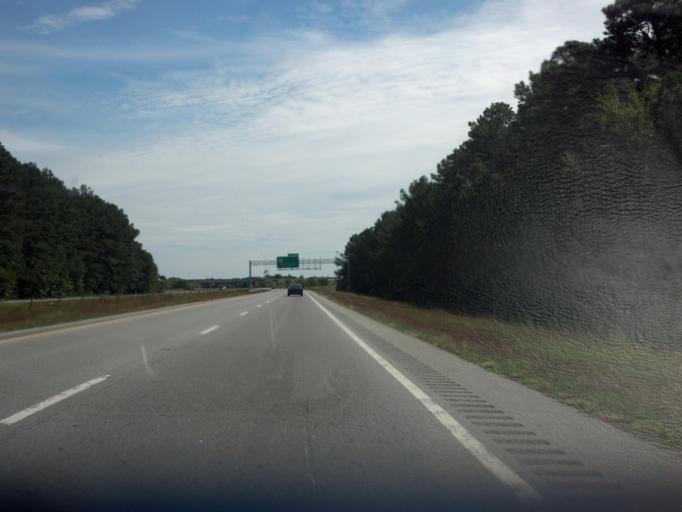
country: US
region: North Carolina
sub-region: Pitt County
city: Summerfield
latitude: 35.6083
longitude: -77.4457
